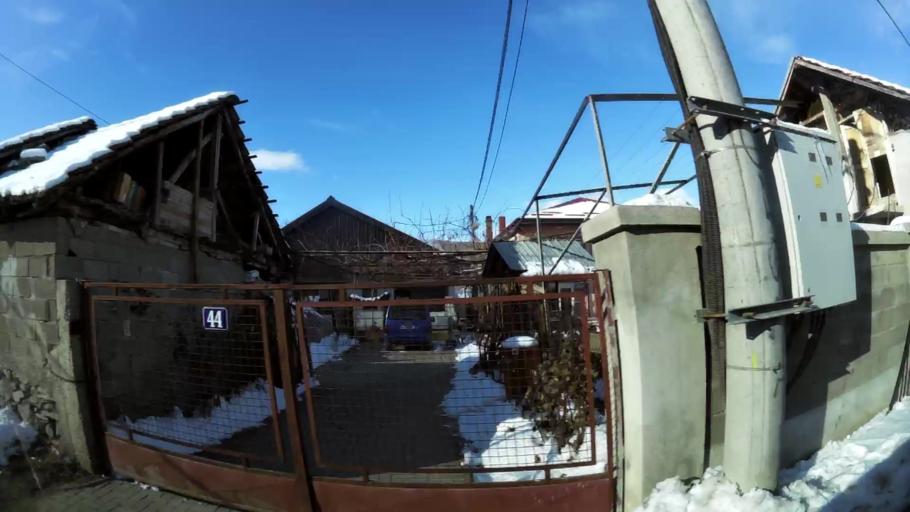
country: MK
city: Grchec
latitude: 41.9744
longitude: 21.3106
